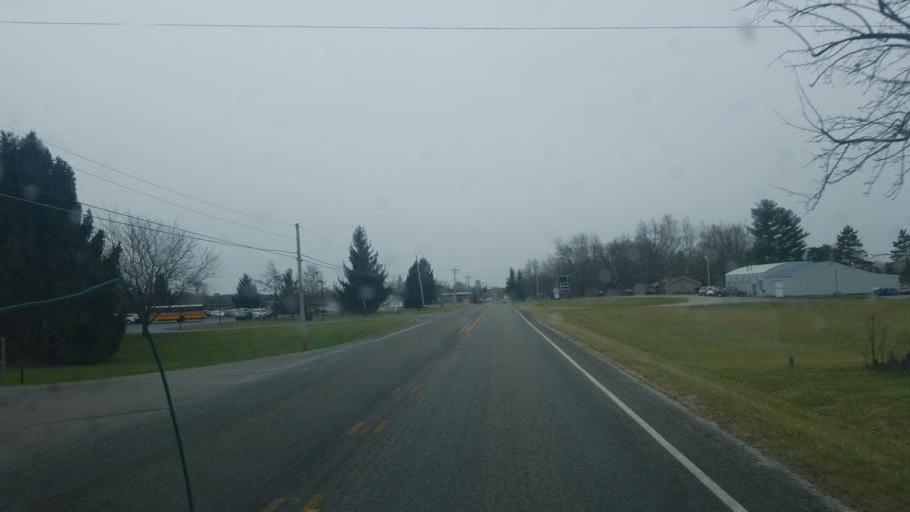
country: US
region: Indiana
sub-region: Henry County
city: Knightstown
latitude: 39.8089
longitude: -85.5323
